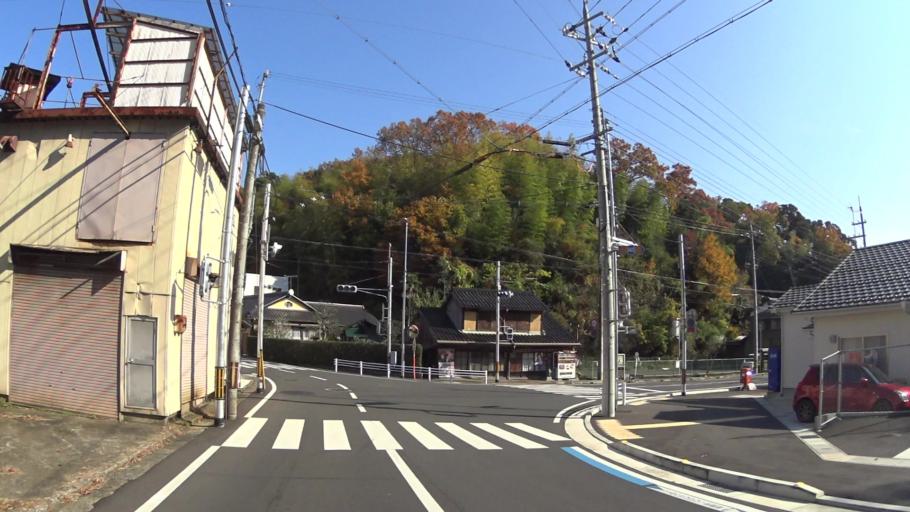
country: JP
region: Kyoto
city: Maizuru
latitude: 35.4806
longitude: 135.3600
